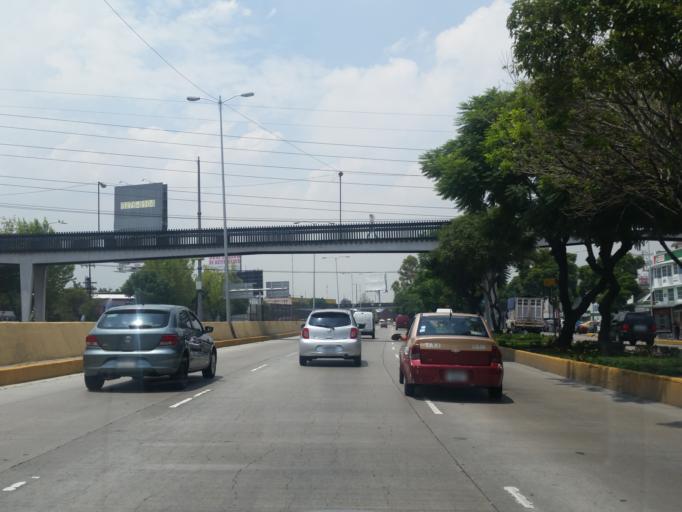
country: MX
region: Mexico City
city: Cuauhtemoc
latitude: 19.4637
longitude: -99.1479
